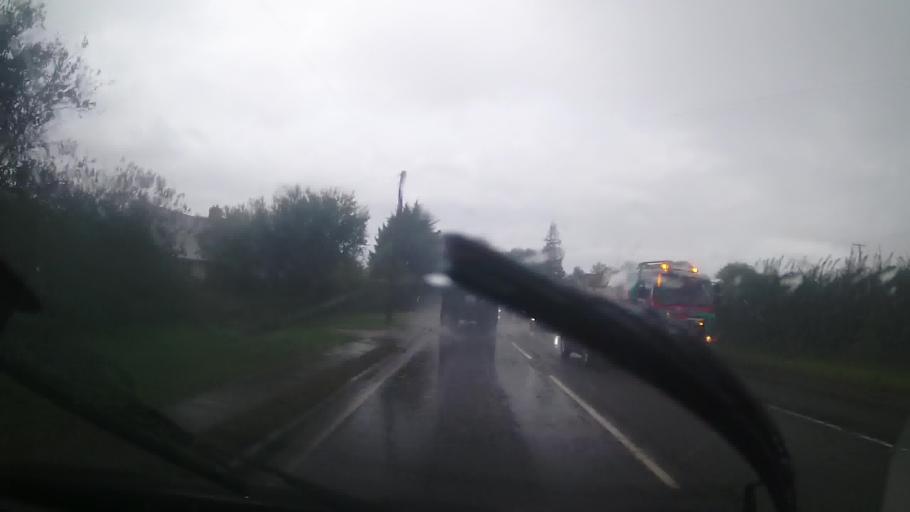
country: GB
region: England
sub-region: Worcestershire
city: Pershore
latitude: 52.1234
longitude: -2.0105
